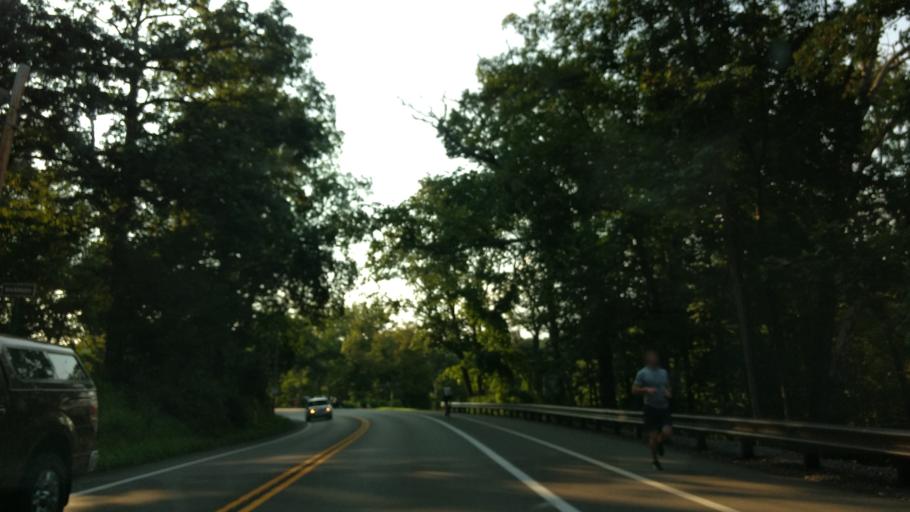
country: US
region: Pennsylvania
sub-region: Allegheny County
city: Gibsonia
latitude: 40.5938
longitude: -80.0062
